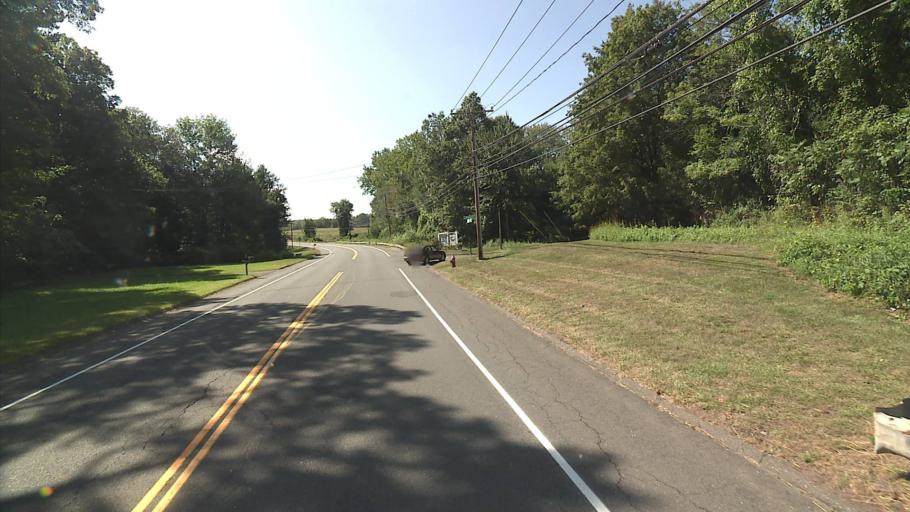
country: US
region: Connecticut
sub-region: Hartford County
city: Blue Hills
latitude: 41.8310
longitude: -72.7539
